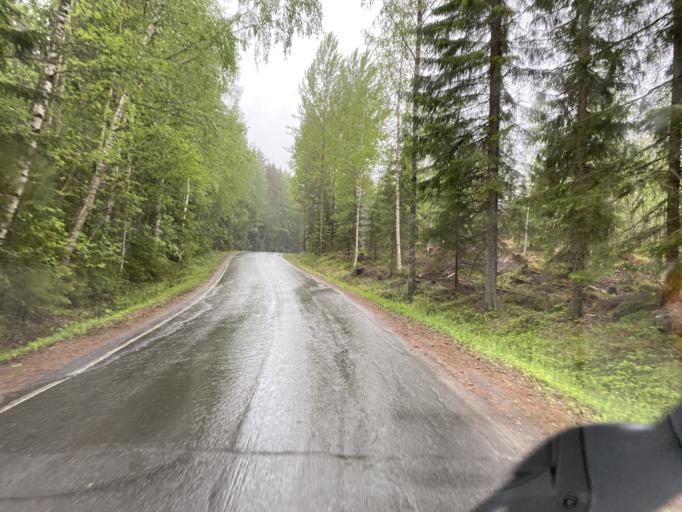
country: FI
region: Haeme
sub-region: Forssa
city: Humppila
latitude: 61.0888
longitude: 23.3088
